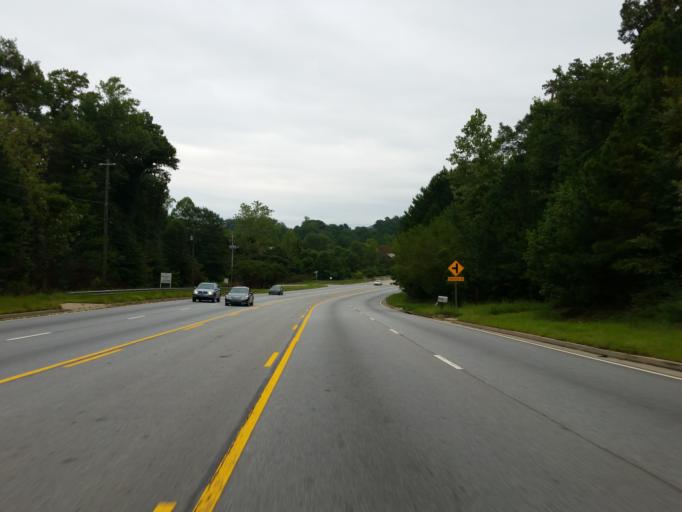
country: US
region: Georgia
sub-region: Cobb County
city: Mableton
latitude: 33.8040
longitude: -84.5242
